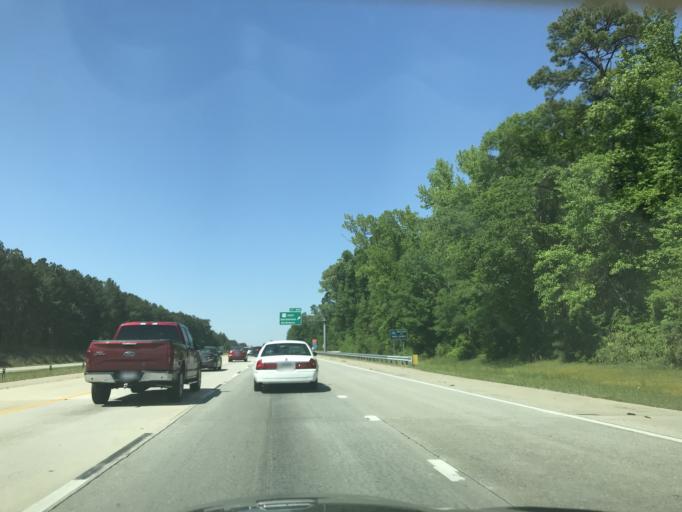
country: US
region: North Carolina
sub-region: Wake County
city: Garner
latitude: 35.6293
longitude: -78.5663
